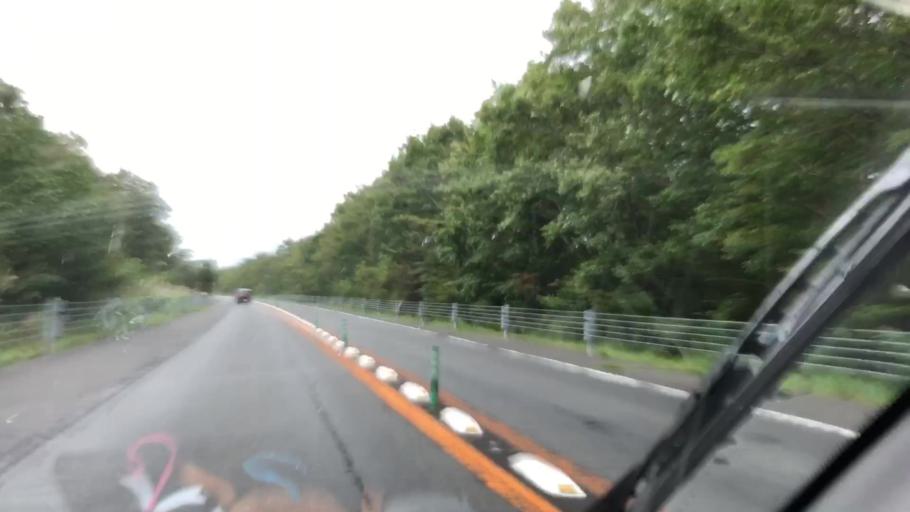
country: JP
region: Shizuoka
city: Gotemba
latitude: 35.4178
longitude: 138.8413
